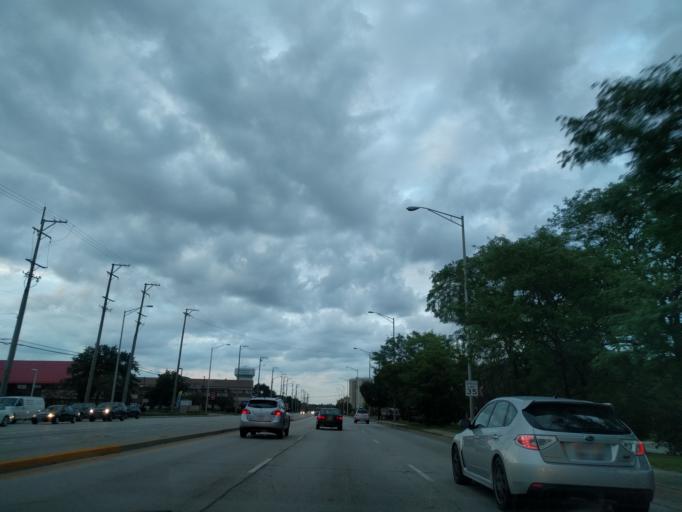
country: US
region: Illinois
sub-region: Cook County
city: Elk Grove Village
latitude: 42.0444
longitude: -87.9831
